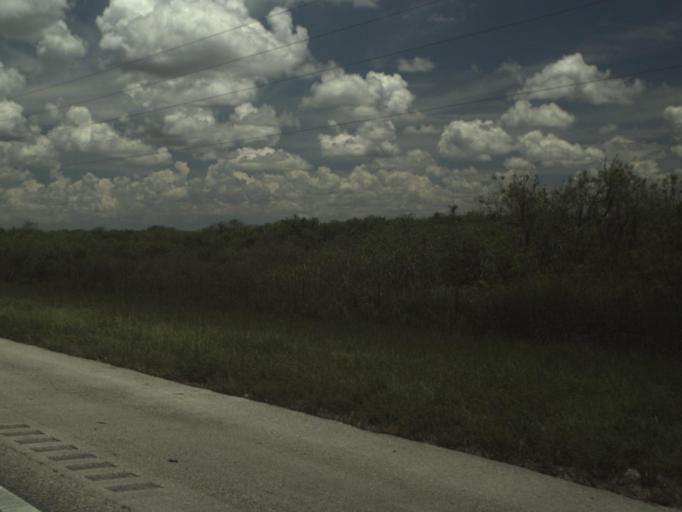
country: US
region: Florida
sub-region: Broward County
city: Weston
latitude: 26.1549
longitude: -80.7554
